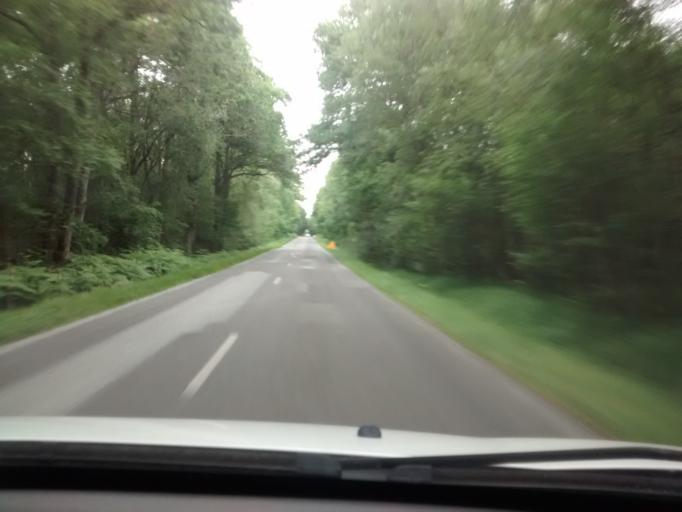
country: FR
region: Brittany
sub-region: Departement d'Ille-et-Vilaine
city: Servon-sur-Vilaine
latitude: 48.1499
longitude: -1.4450
